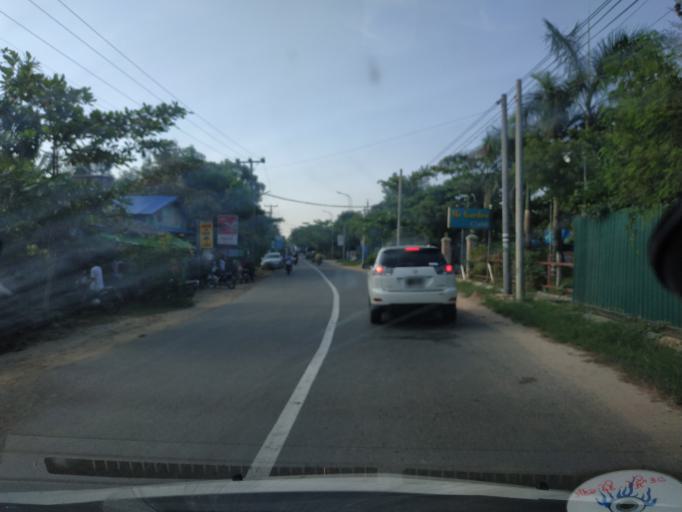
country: MM
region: Ayeyarwady
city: Pathein
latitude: 16.8139
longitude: 94.7532
